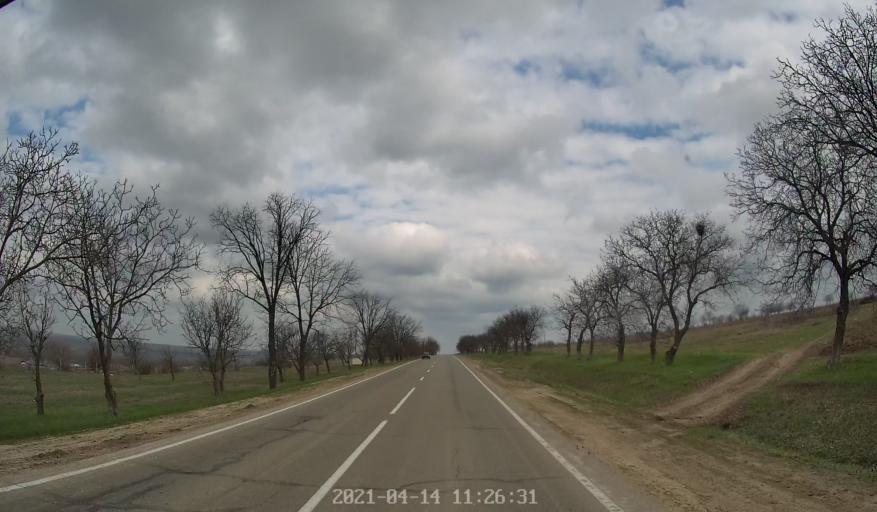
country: MD
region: Criuleni
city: Criuleni
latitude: 47.1647
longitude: 29.1634
